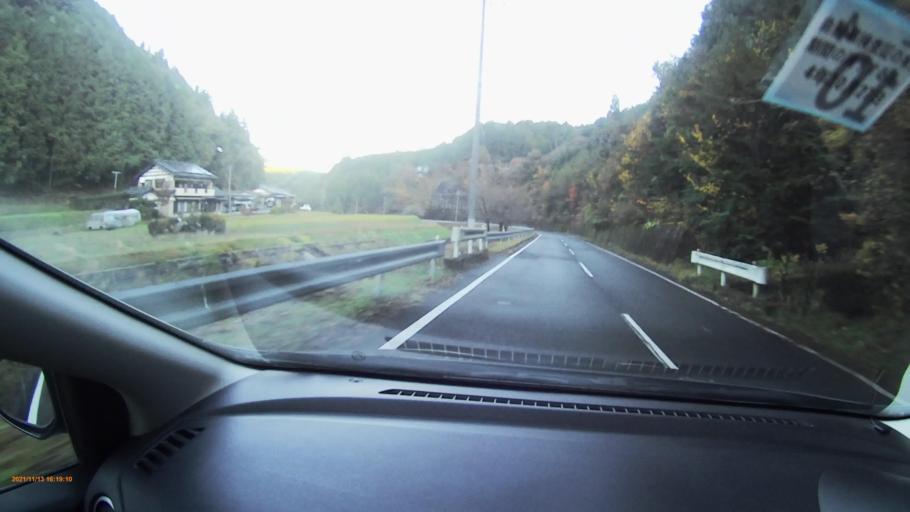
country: JP
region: Gifu
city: Nakatsugawa
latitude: 35.5696
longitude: 137.5058
